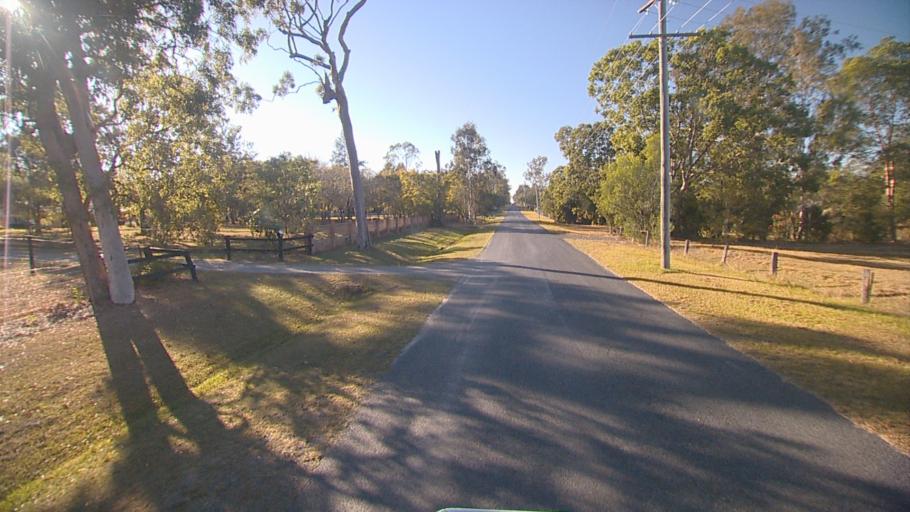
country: AU
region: Queensland
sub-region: Logan
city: North Maclean
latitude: -27.7877
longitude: 152.9664
